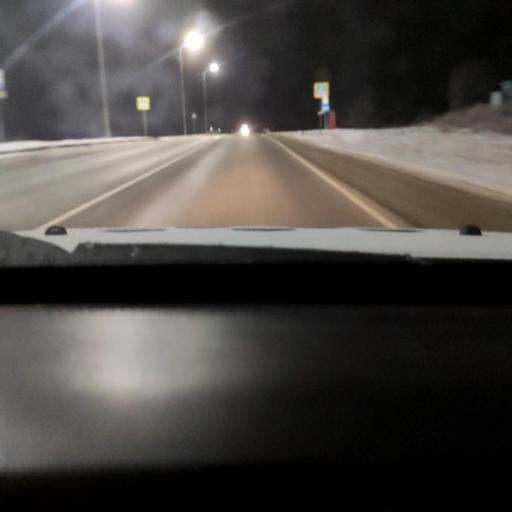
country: RU
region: Perm
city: Pavlovskiy
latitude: 57.8912
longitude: 54.9363
